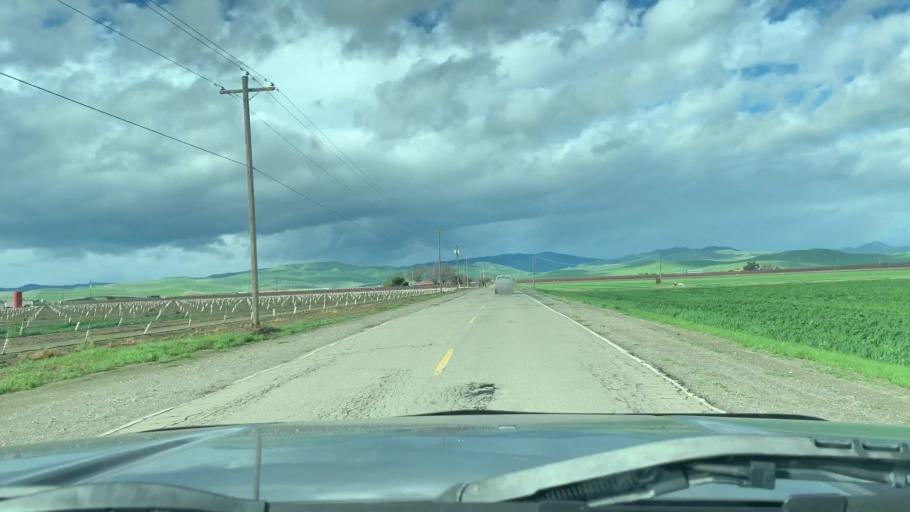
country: US
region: California
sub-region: Merced County
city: Gustine
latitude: 37.1224
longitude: -121.0050
